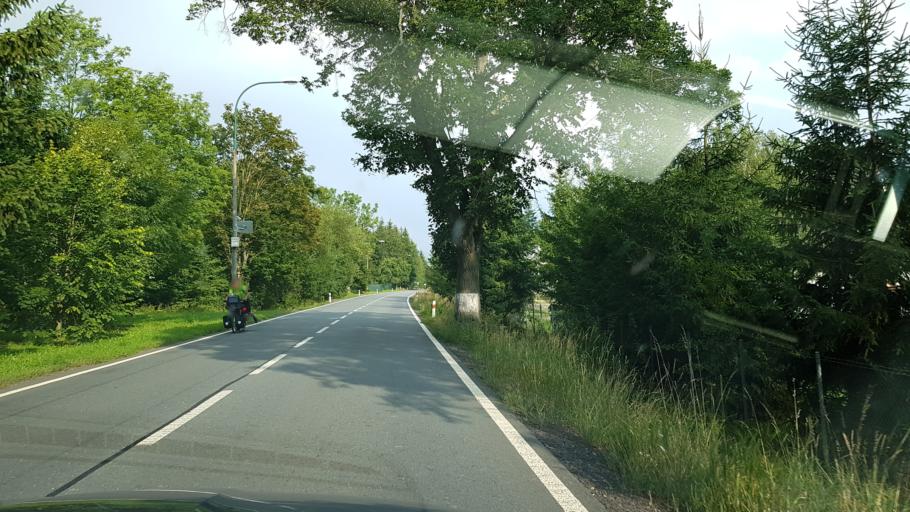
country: CZ
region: Pardubicky
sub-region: Okres Usti nad Orlici
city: Kraliky
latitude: 50.0888
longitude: 16.7217
